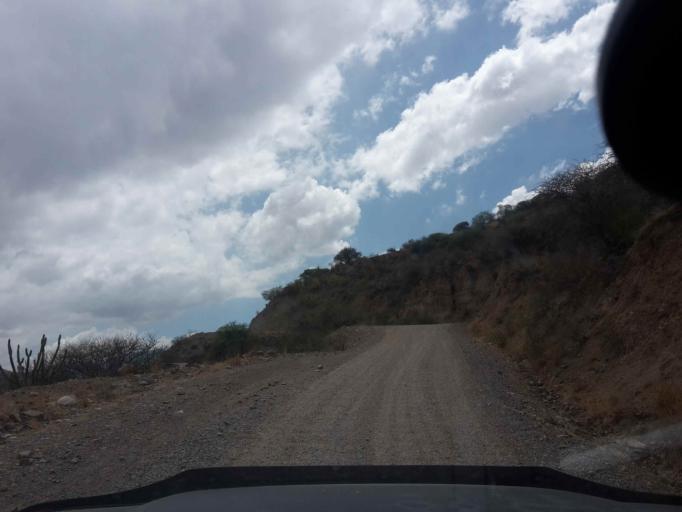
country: BO
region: Cochabamba
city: Sipe Sipe
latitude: -17.5507
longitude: -66.4778
